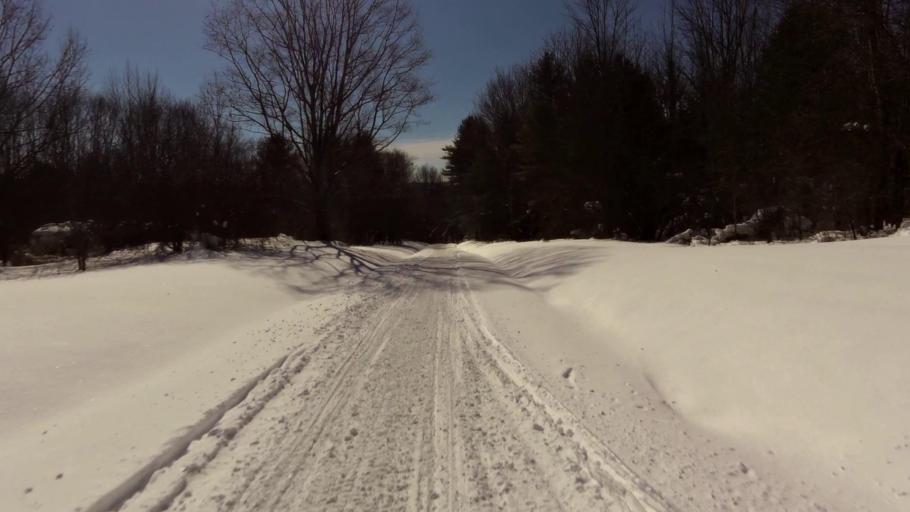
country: US
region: New York
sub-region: Allegany County
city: Cuba
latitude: 42.2933
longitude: -78.2391
